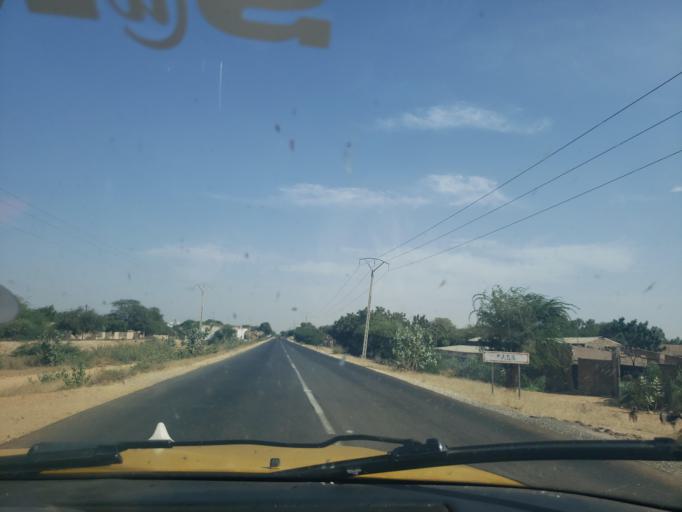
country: SN
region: Saint-Louis
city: Saint-Louis
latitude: 15.9300
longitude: -16.3284
